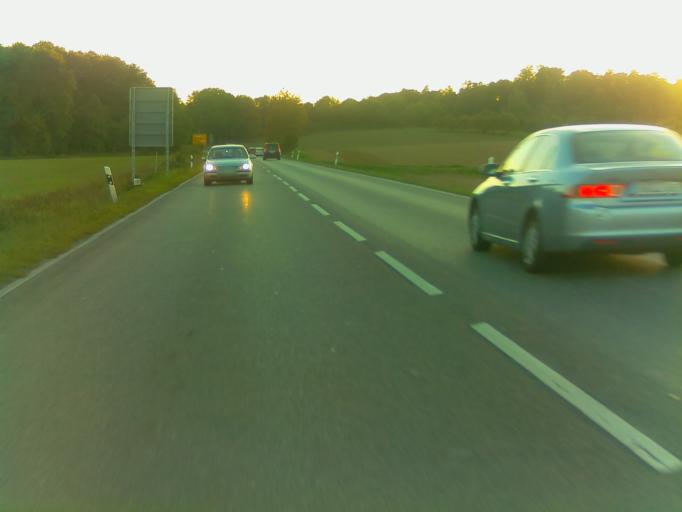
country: DE
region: Hesse
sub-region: Regierungsbezirk Darmstadt
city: Rosbach vor der Hohe
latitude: 50.2851
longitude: 8.6655
